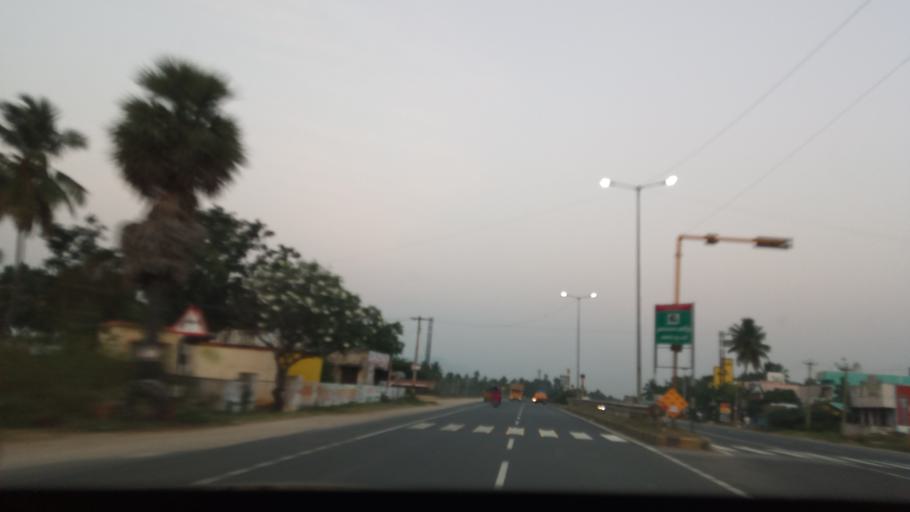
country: IN
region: Tamil Nadu
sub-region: Salem
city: Belur
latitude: 11.6578
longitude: 78.4217
